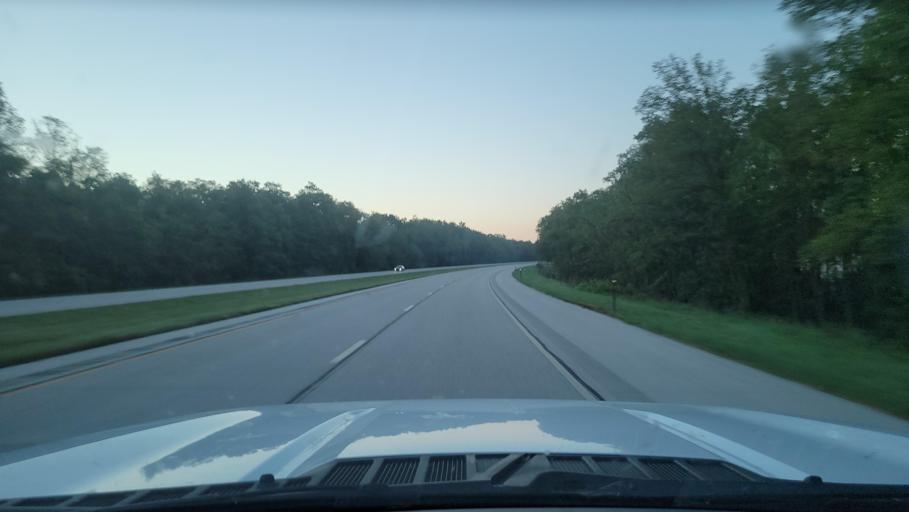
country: US
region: Illinois
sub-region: Adams County
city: Payson
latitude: 39.8296
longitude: -91.3043
